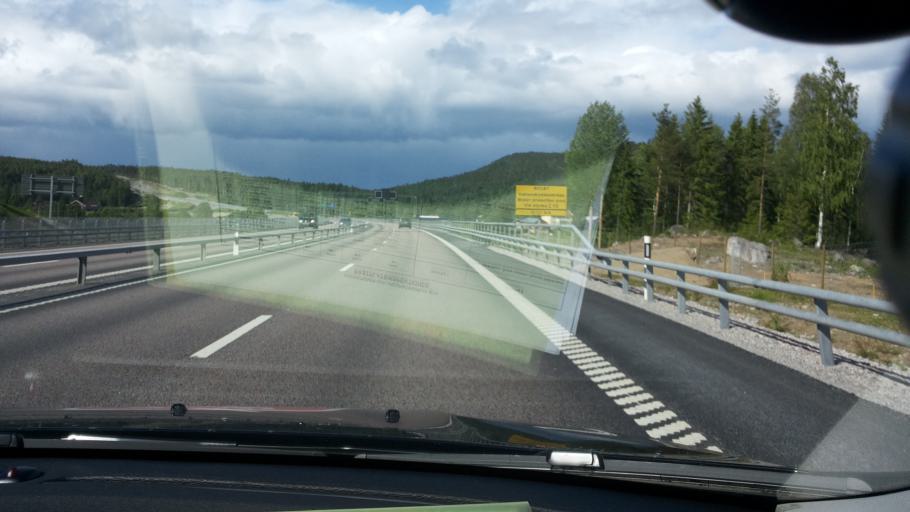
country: SE
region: Vaesternorrland
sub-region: Sundsvalls Kommun
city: Nolby
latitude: 62.2874
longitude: 17.3487
